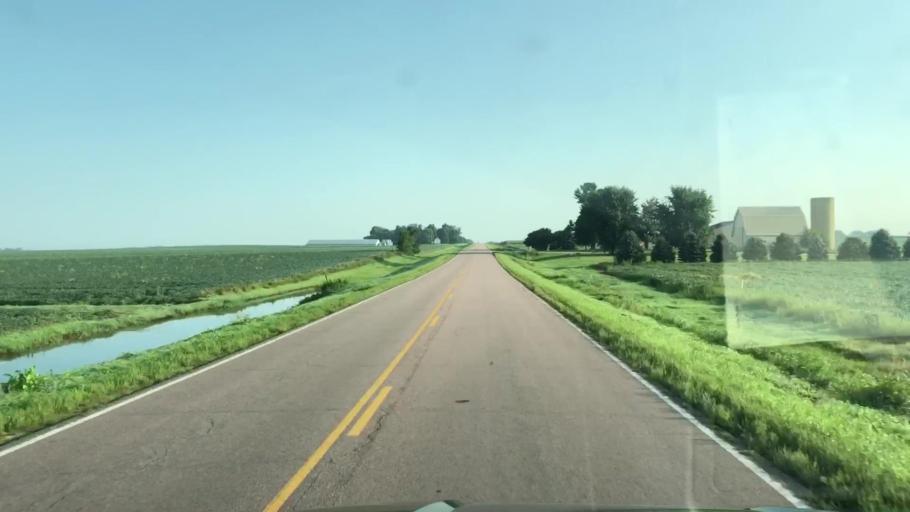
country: US
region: Iowa
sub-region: Lyon County
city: George
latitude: 43.2747
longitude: -95.9998
